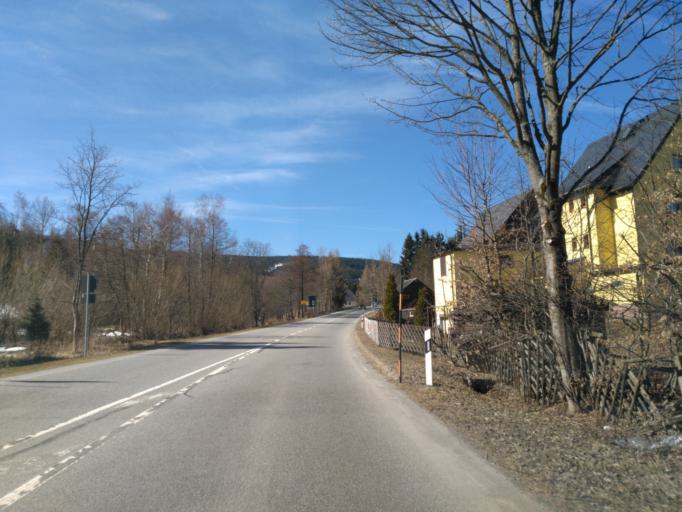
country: DE
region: Saxony
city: Kurort Oberwiesenthal
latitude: 50.4190
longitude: 12.9795
